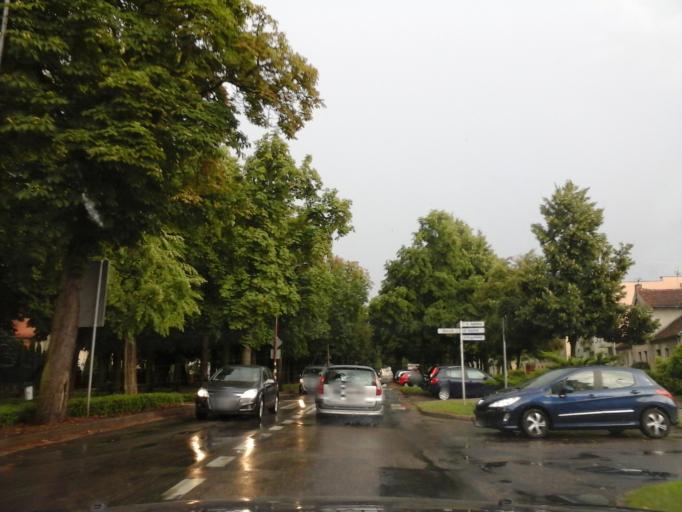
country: PL
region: Greater Poland Voivodeship
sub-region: Powiat miedzychodzki
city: Miedzychod
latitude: 52.6002
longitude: 15.8907
